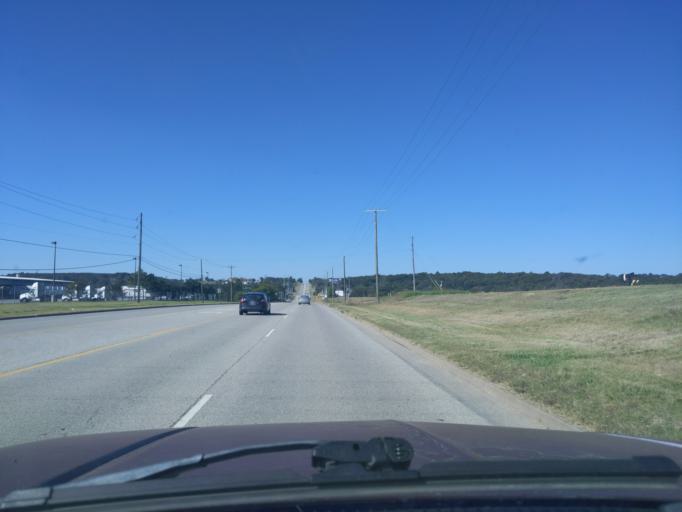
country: US
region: Oklahoma
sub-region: Tulsa County
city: Glenpool
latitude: 35.9884
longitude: -96.0251
